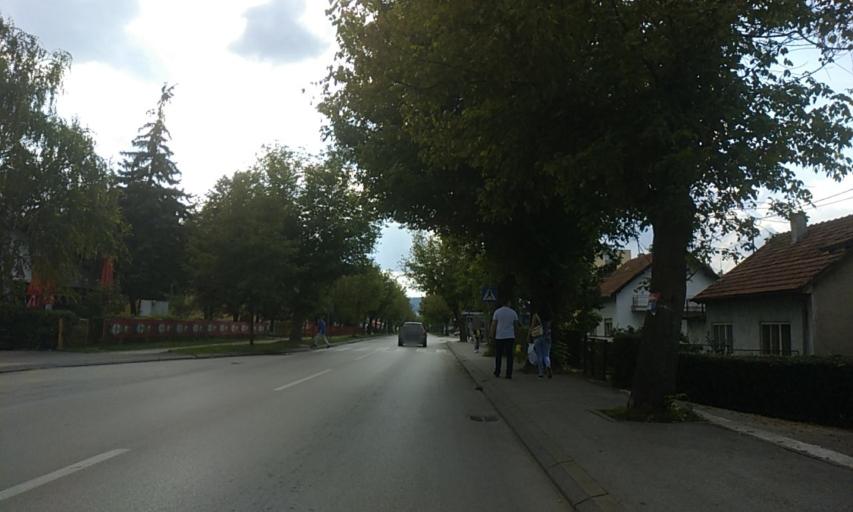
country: BA
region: Republika Srpska
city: Mejdan - Obilicevo
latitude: 44.7639
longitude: 17.1978
